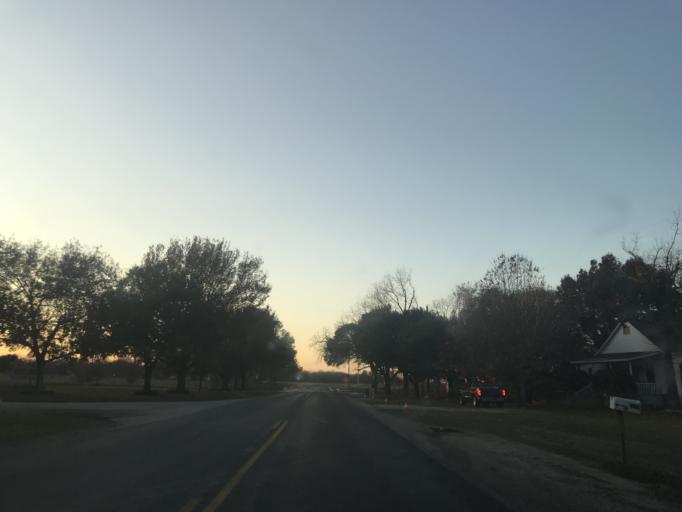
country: US
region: Texas
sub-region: Williamson County
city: Hutto
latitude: 30.4948
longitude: -97.4974
